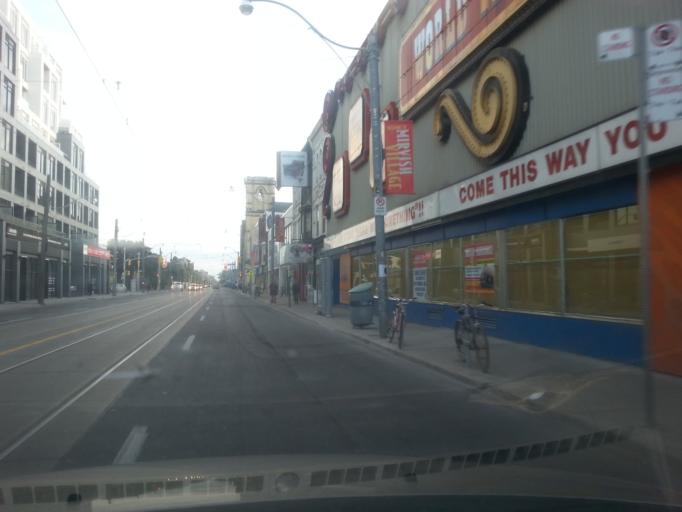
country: CA
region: Ontario
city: Toronto
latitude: 43.6647
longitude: -79.4111
